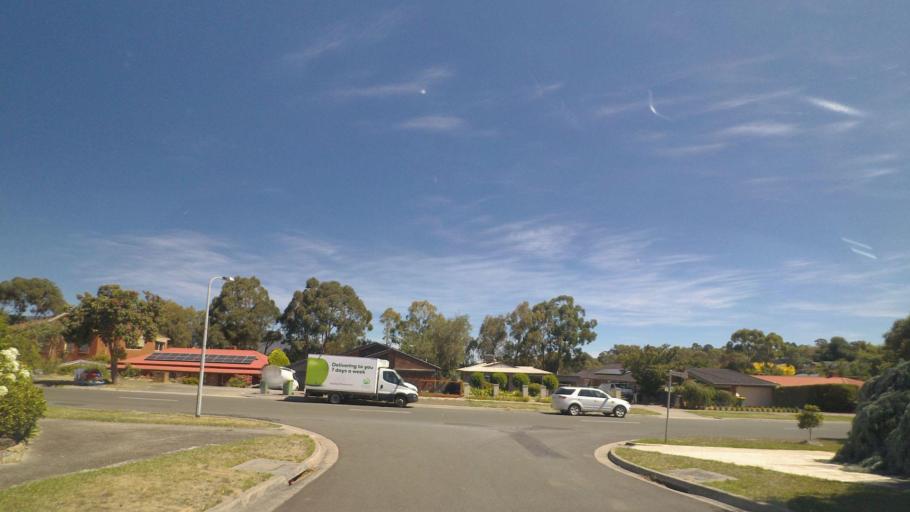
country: AU
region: Victoria
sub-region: Yarra Ranges
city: Lilydale
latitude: -37.7700
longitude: 145.3289
